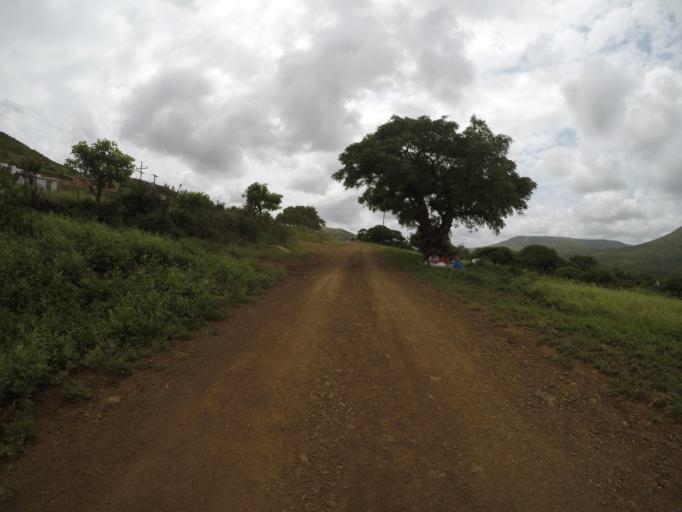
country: ZA
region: KwaZulu-Natal
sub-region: uThungulu District Municipality
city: Empangeni
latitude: -28.5937
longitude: 31.8811
